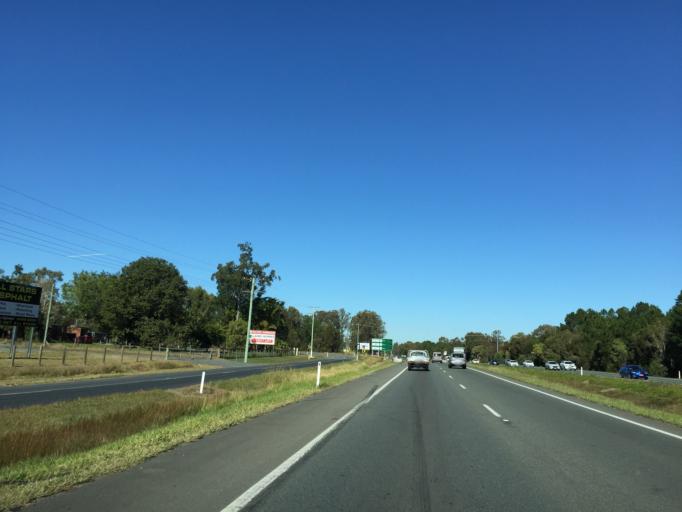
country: AU
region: Queensland
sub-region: Moreton Bay
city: Caboolture
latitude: -27.0508
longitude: 152.9772
